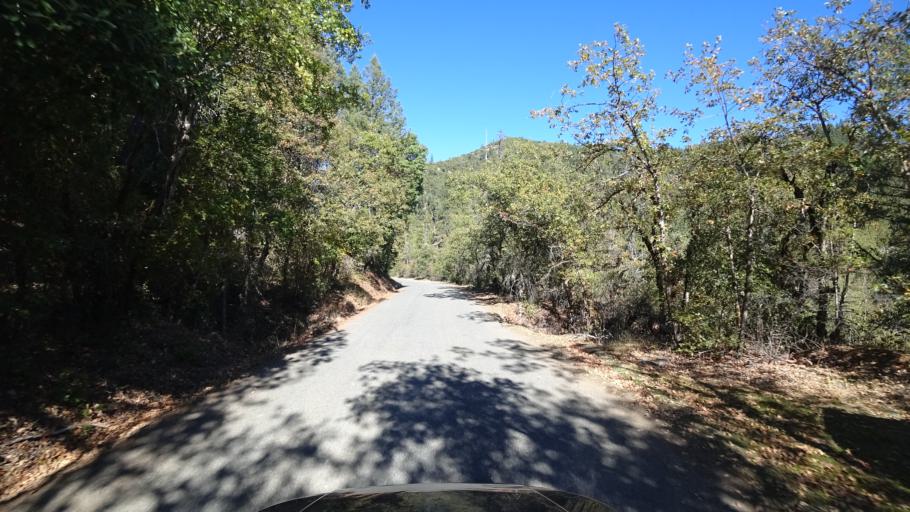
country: US
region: California
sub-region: Humboldt County
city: Willow Creek
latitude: 41.2415
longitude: -123.2834
